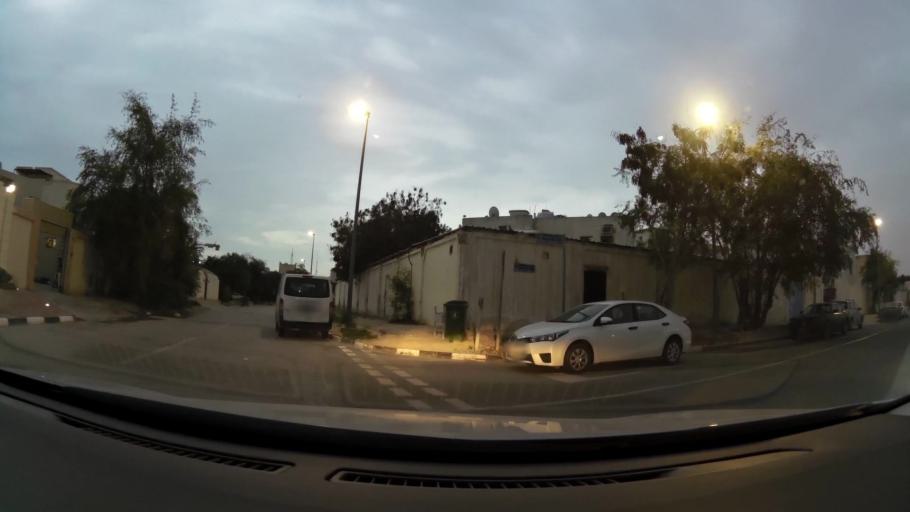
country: QA
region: Baladiyat ad Dawhah
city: Doha
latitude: 25.3453
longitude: 51.5134
